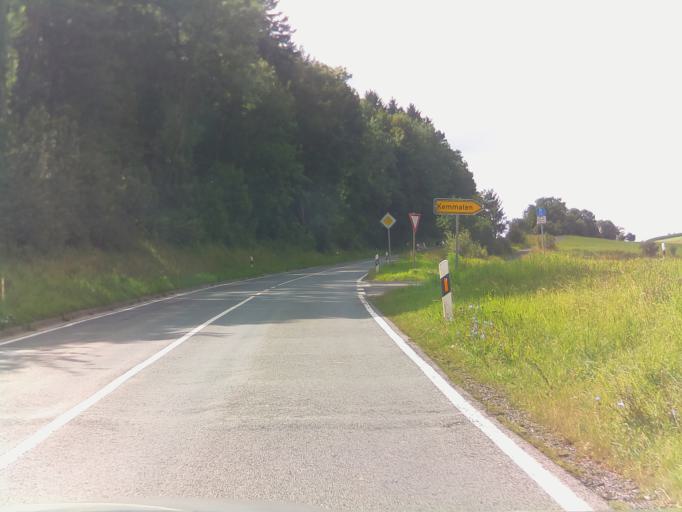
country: DE
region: Bavaria
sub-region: Upper Franconia
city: Neustadt bei Coburg
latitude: 50.2926
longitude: 11.0938
